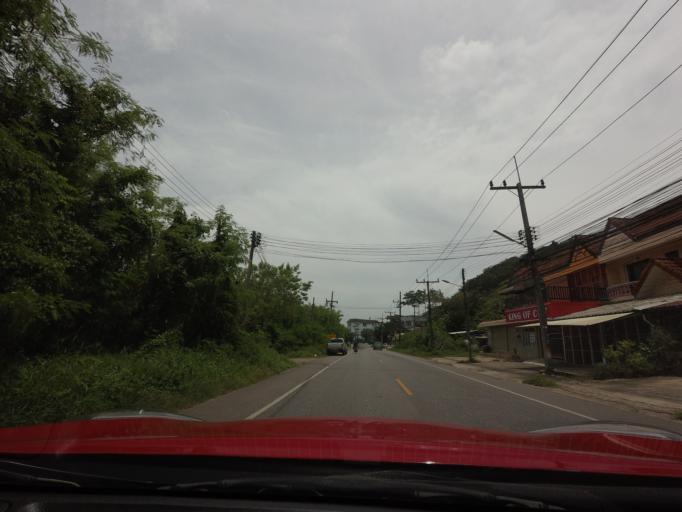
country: TH
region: Songkhla
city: Hat Yai
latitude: 6.9991
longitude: 100.5152
